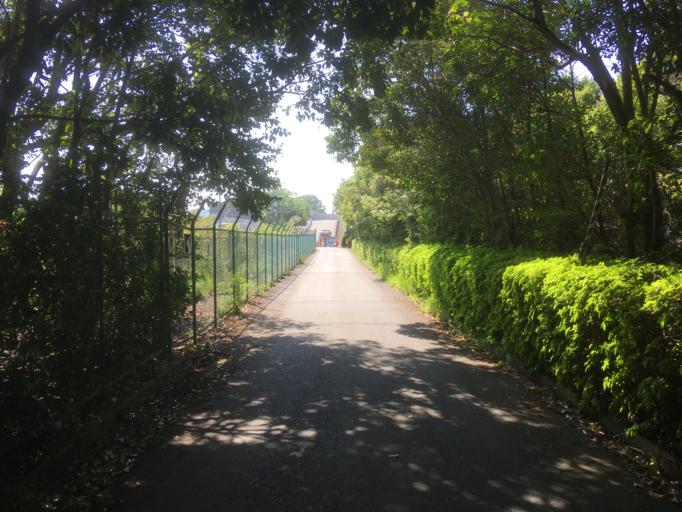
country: JP
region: Nara
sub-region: Ikoma-shi
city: Ikoma
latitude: 34.7329
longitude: 135.7153
